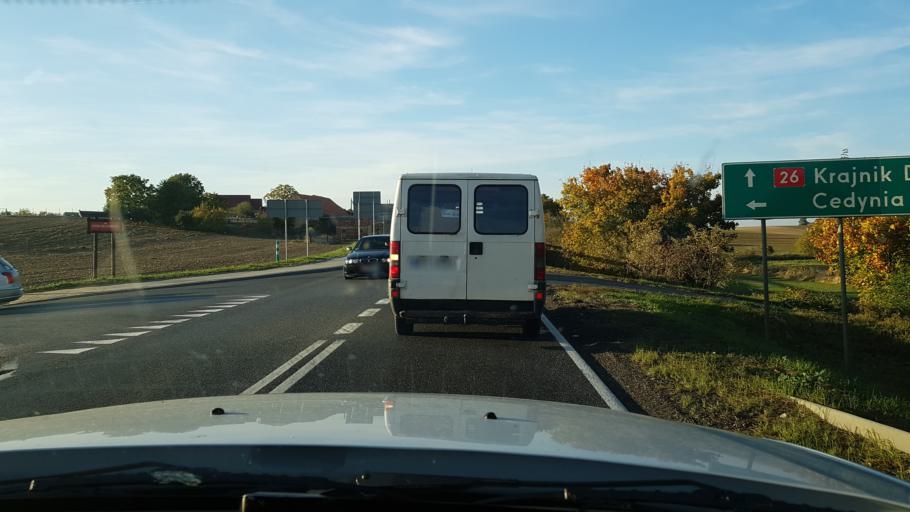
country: DE
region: Brandenburg
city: Schwedt (Oder)
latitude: 53.0250
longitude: 14.3242
